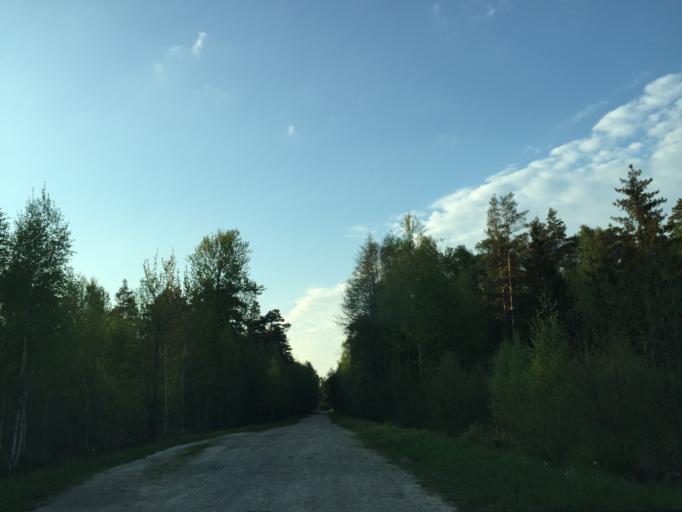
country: LV
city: Tireli
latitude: 56.8881
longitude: 23.6900
